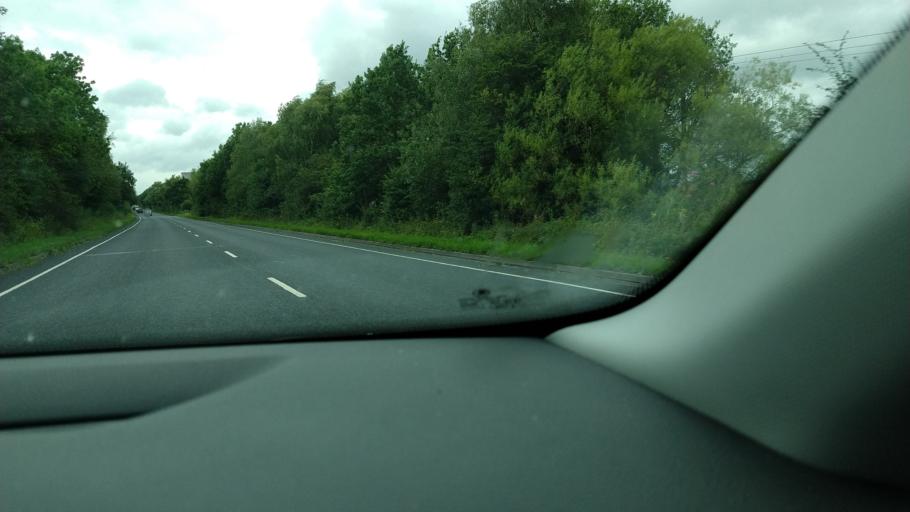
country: GB
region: England
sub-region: East Riding of Yorkshire
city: Barmby on the Marsh
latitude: 53.7162
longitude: -0.9635
